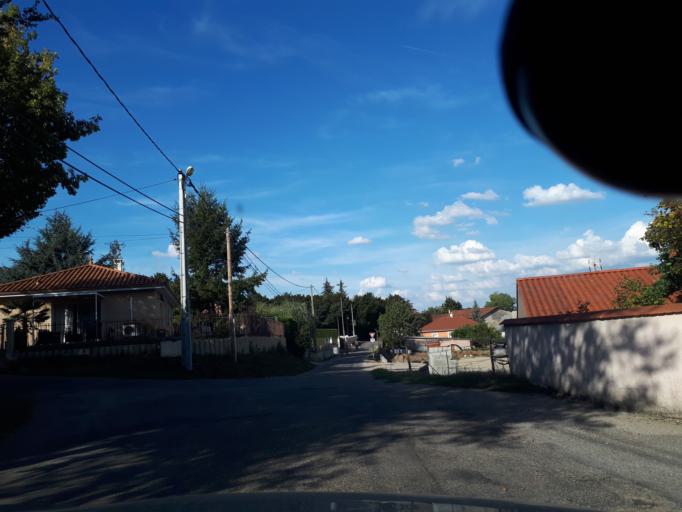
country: FR
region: Rhone-Alpes
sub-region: Departement de l'Isere
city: Maubec
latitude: 45.5233
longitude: 5.2534
